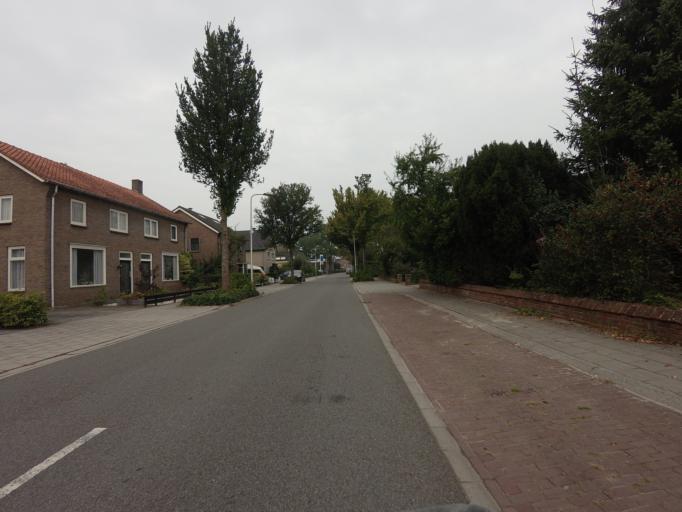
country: NL
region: Overijssel
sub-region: Gemeente Deventer
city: Schalkhaar
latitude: 52.2661
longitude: 6.1960
